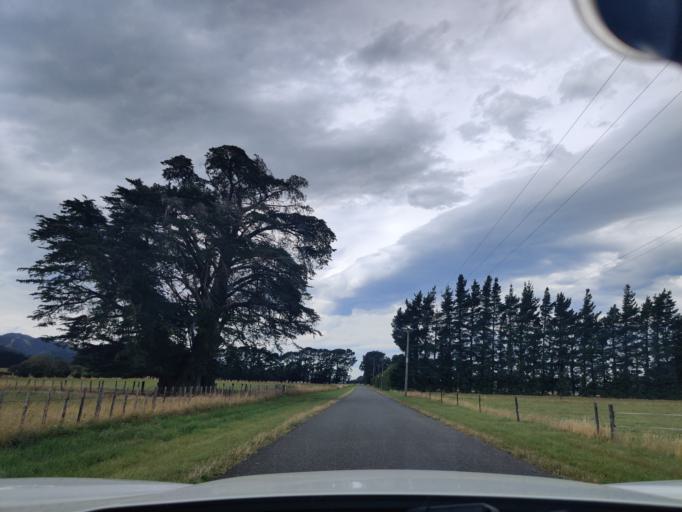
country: NZ
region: Wellington
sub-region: Masterton District
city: Masterton
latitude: -41.0267
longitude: 175.4536
